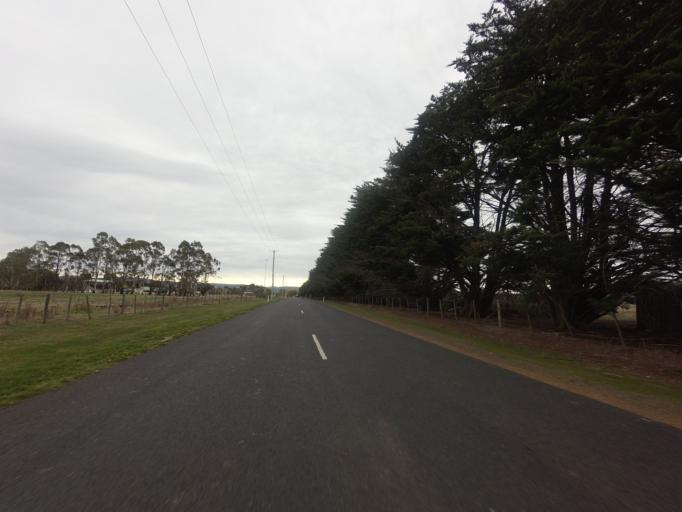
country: AU
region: Tasmania
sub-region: Derwent Valley
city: New Norfolk
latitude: -42.3894
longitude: 147.0062
